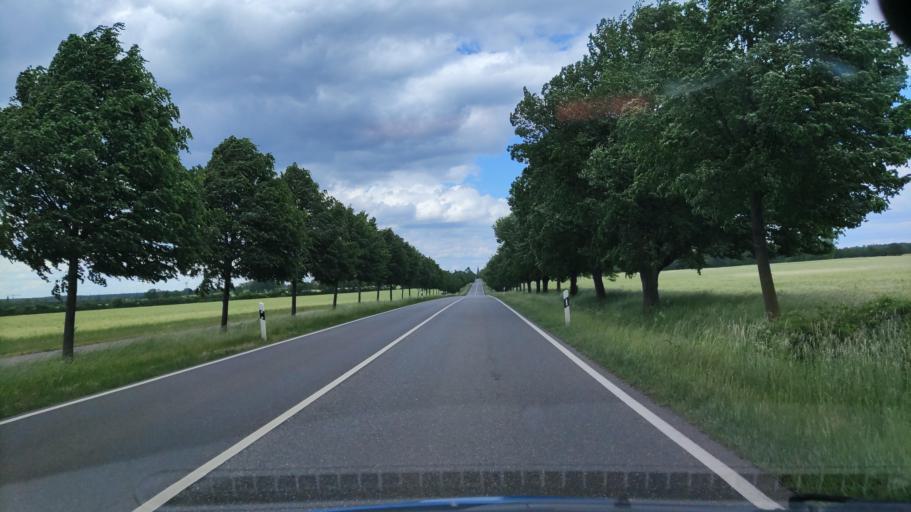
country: DE
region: Mecklenburg-Vorpommern
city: Spornitz
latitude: 53.3987
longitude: 11.6982
